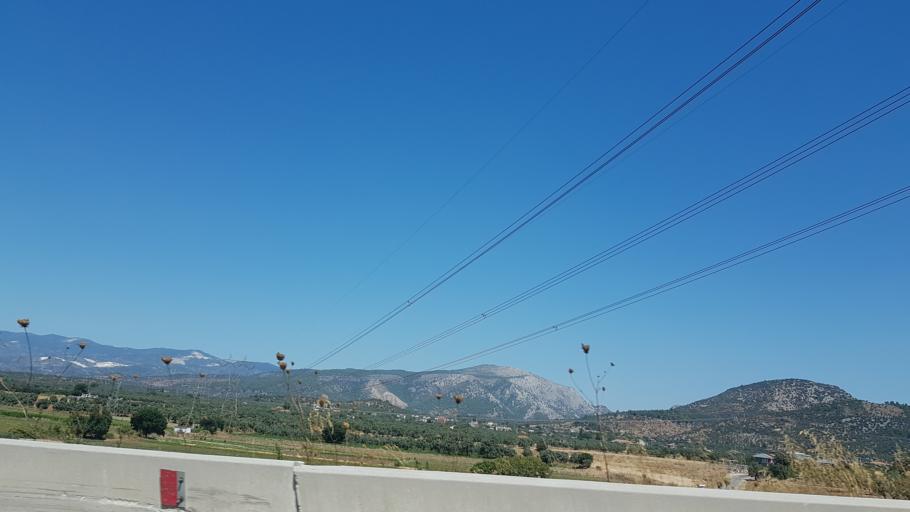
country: TR
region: Mugla
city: Milas
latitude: 37.2879
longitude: 27.8096
